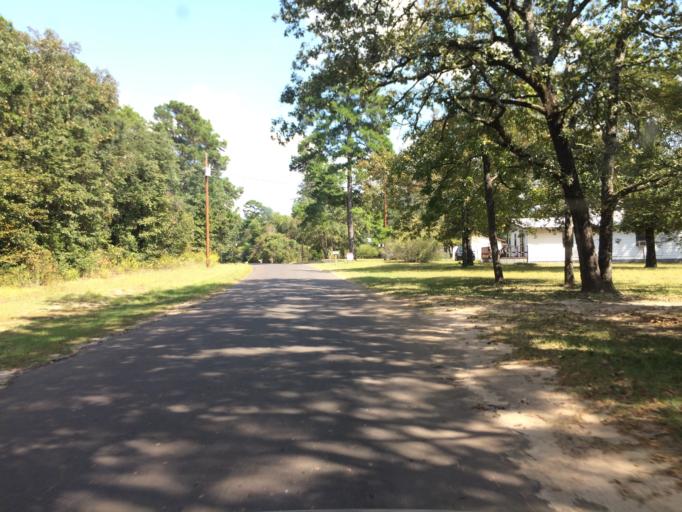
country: US
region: Texas
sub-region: Wood County
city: Hawkins
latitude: 32.6558
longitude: -95.2164
